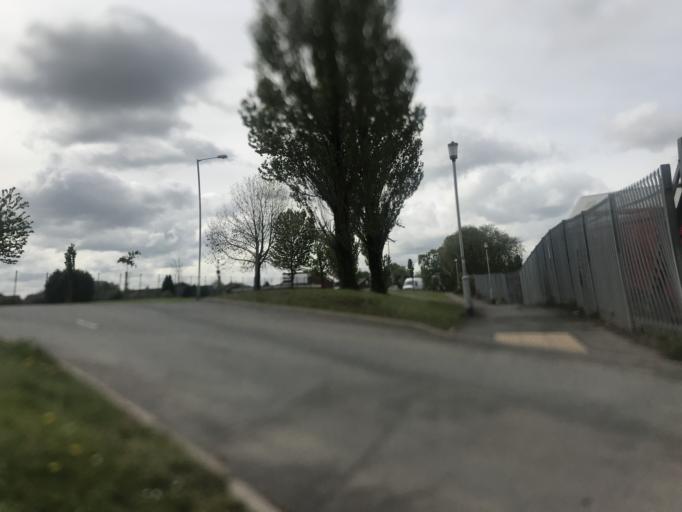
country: GB
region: England
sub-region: Borough of Stockport
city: Stockport
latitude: 53.3942
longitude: -2.1660
